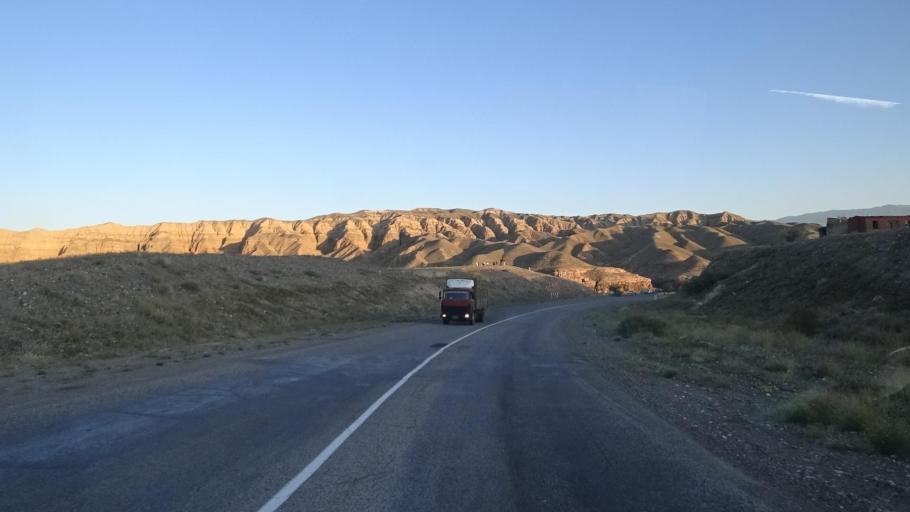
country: KZ
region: Almaty Oblysy
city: Kegen
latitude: 43.2714
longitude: 78.9716
